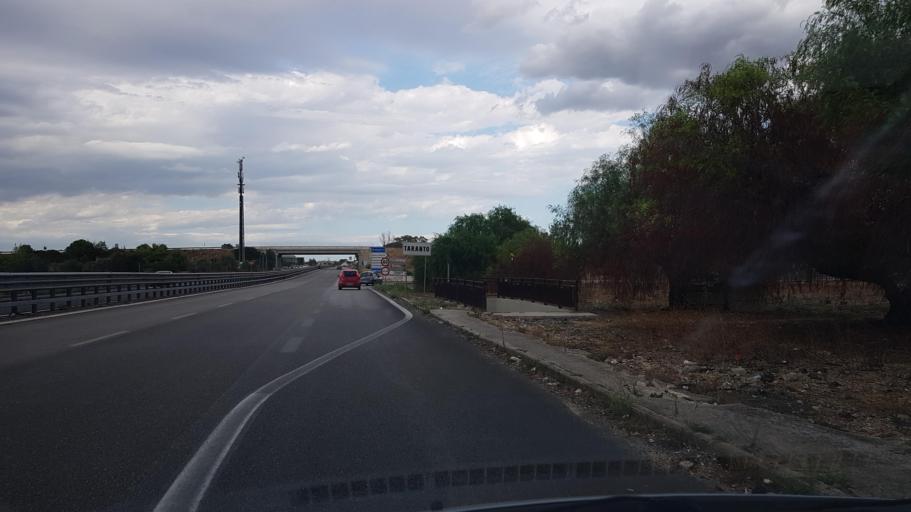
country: IT
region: Apulia
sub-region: Provincia di Taranto
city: Paolo VI
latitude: 40.5195
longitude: 17.2593
